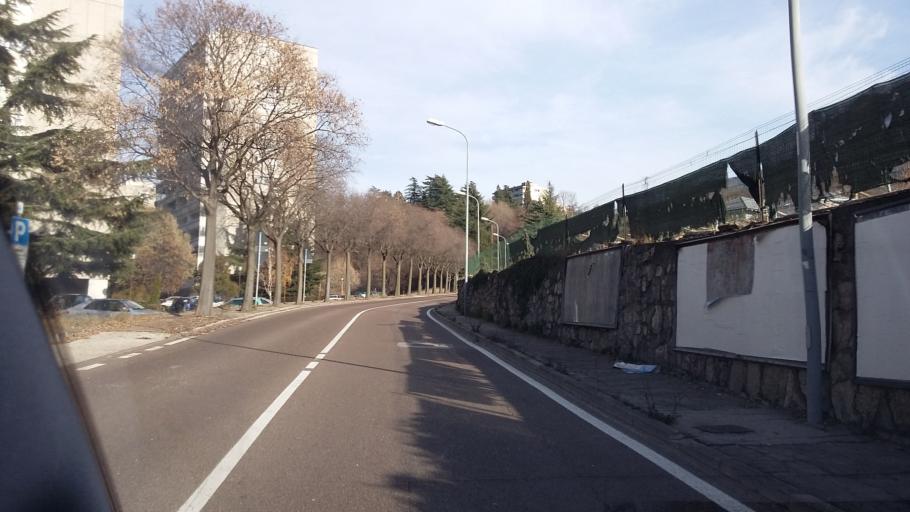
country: IT
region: Trentino-Alto Adige
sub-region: Provincia di Trento
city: Ravina
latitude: 46.0383
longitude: 11.1343
